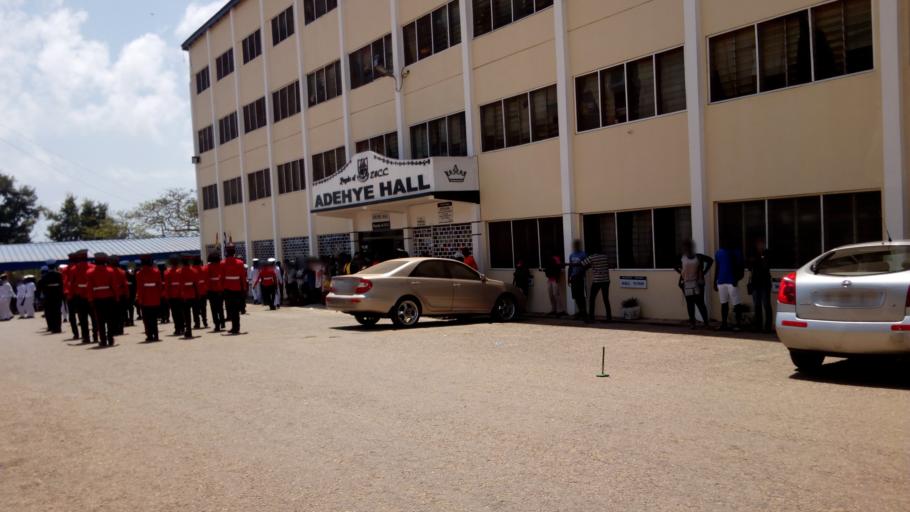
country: GH
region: Central
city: Cape Coast
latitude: 5.1056
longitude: -1.2863
